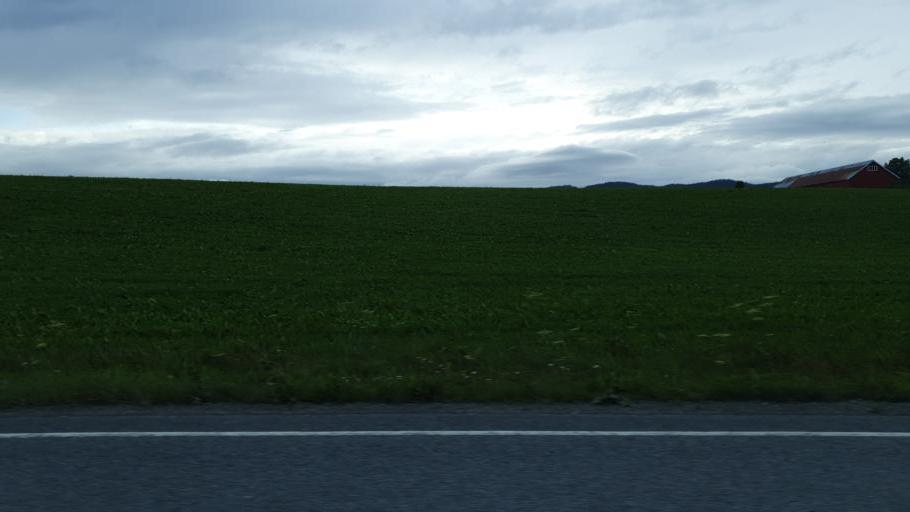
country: NO
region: Sor-Trondelag
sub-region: Melhus
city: Lundamo
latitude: 63.2164
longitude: 10.3068
